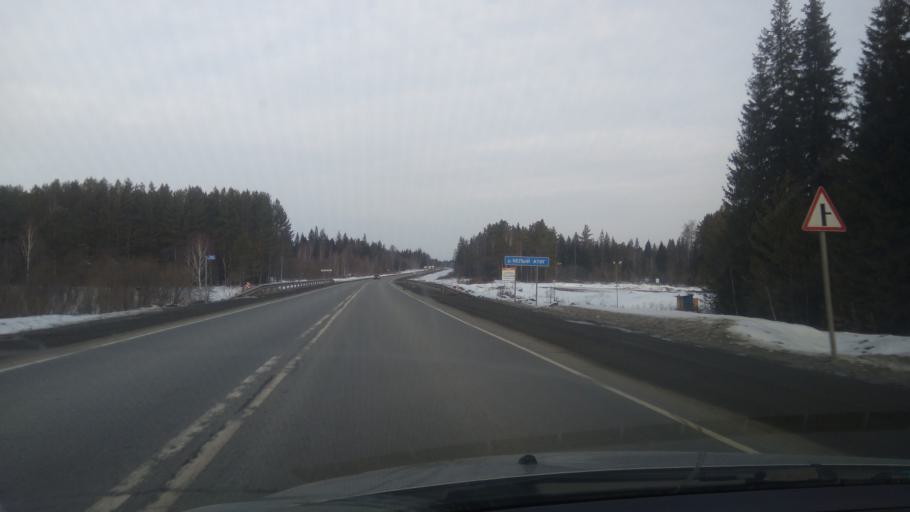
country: RU
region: Sverdlovsk
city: Atig
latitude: 56.8032
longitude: 59.3774
